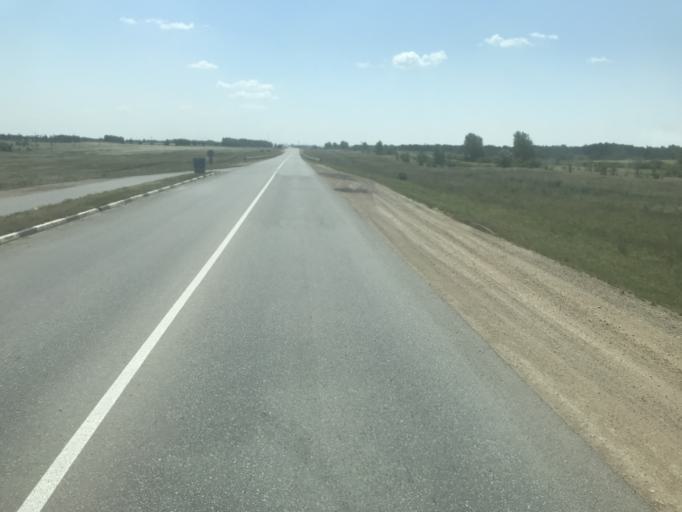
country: KZ
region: Aqmola
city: Kokshetau
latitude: 53.4125
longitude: 69.4261
